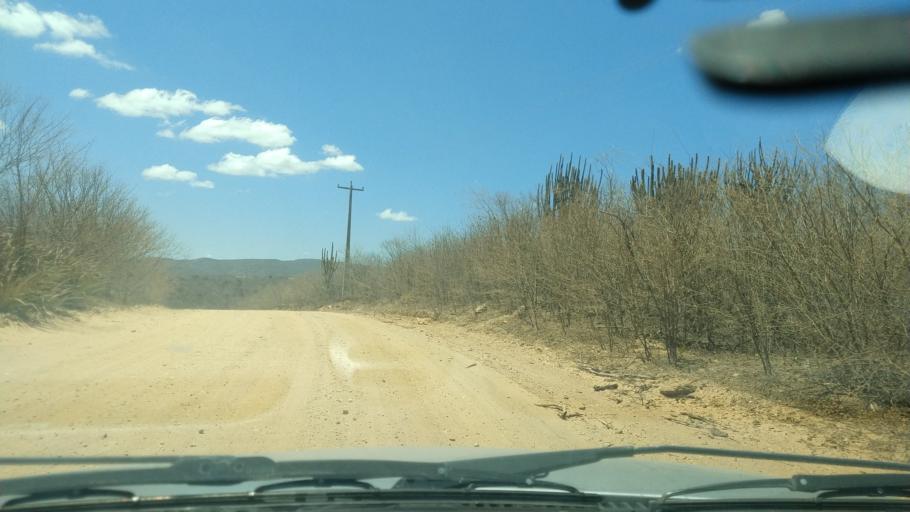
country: BR
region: Rio Grande do Norte
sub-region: Cerro Cora
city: Cerro Cora
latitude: -6.0092
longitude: -36.2865
